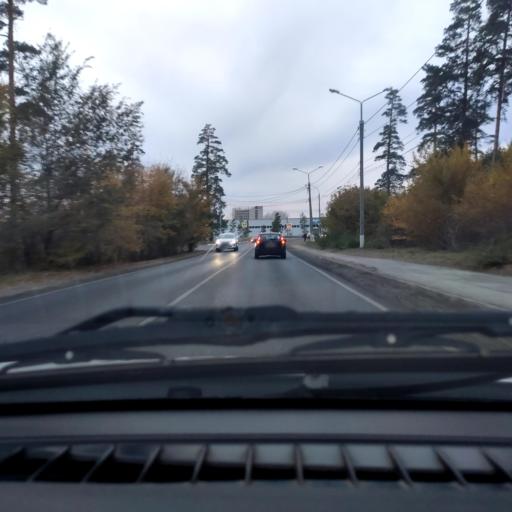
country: RU
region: Samara
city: Tol'yatti
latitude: 53.4763
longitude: 49.3282
